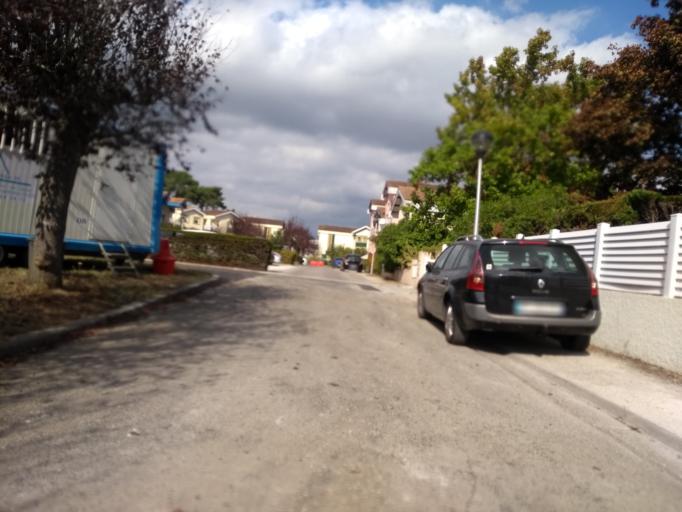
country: FR
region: Aquitaine
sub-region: Departement de la Gironde
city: Gradignan
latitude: 44.7841
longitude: -0.6027
